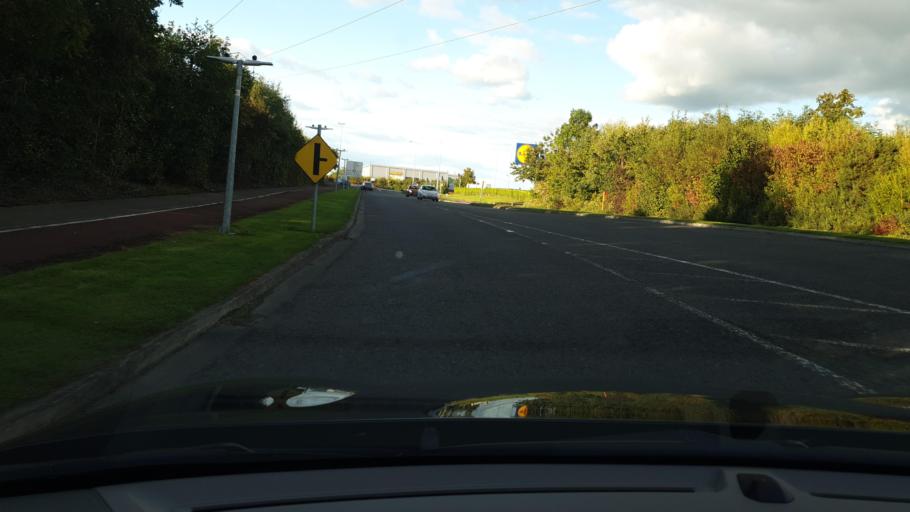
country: IE
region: Leinster
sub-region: Kildare
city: Naas
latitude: 53.2100
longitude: -6.7001
